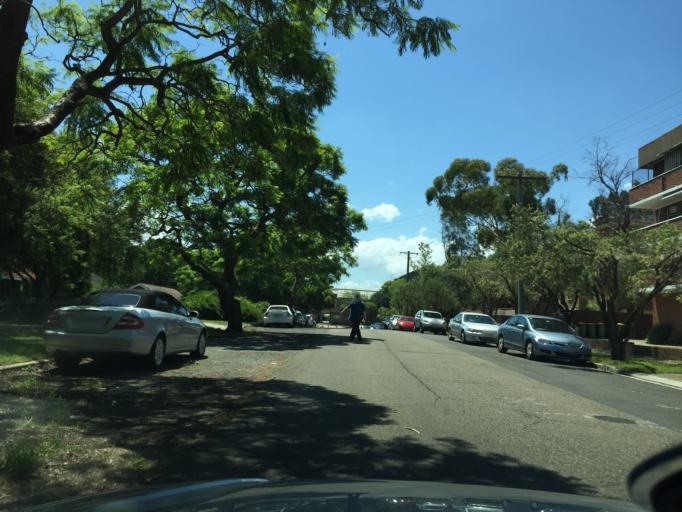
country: AU
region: New South Wales
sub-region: Parramatta
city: City of Parramatta
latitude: -33.8011
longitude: 151.0018
